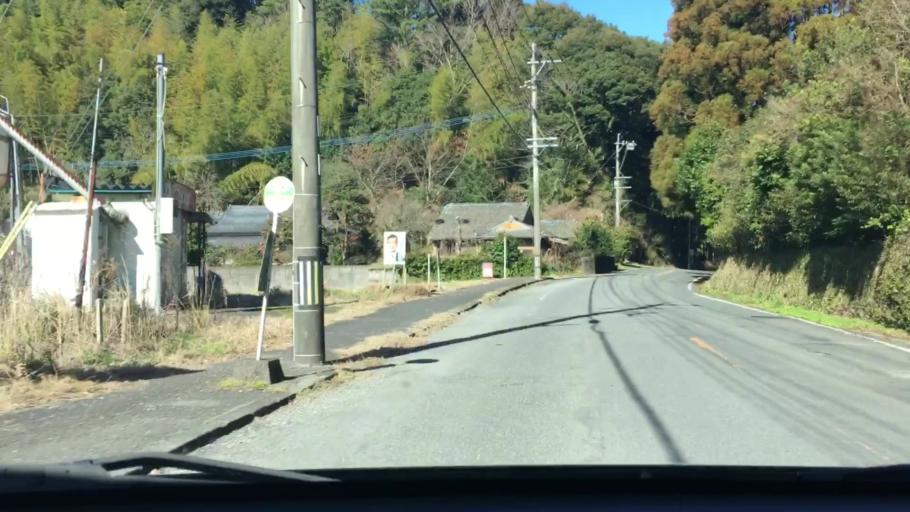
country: JP
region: Kagoshima
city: Satsumasendai
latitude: 31.7808
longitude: 130.3989
